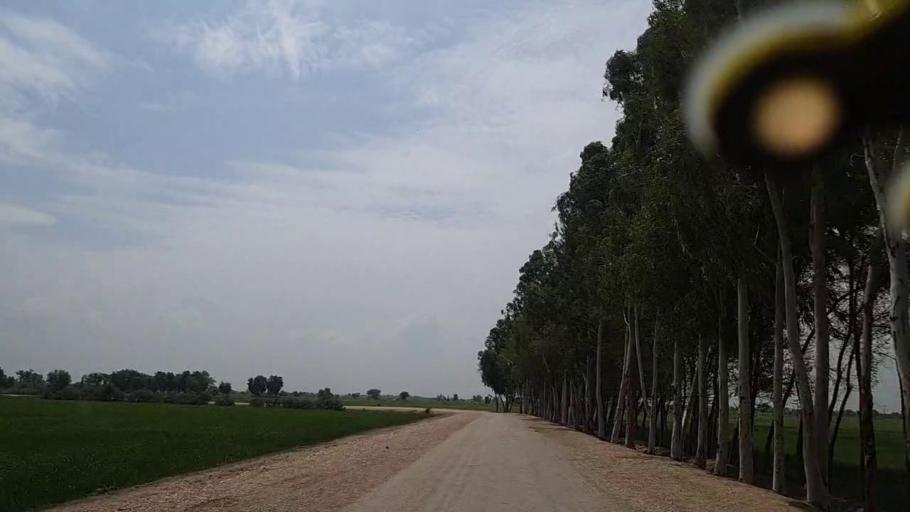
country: PK
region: Sindh
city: Rustam jo Goth
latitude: 28.1097
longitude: 68.8697
